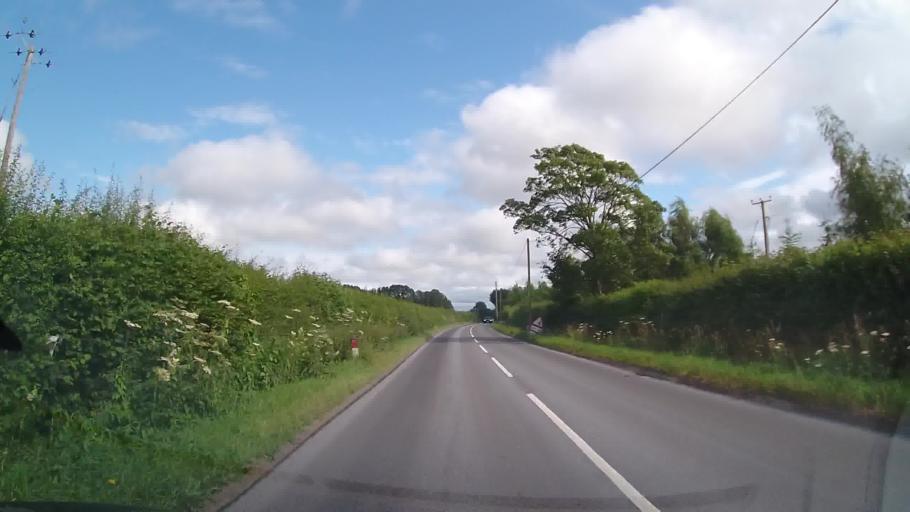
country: GB
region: England
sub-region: Shropshire
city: Pant
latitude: 52.8049
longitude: -3.0254
